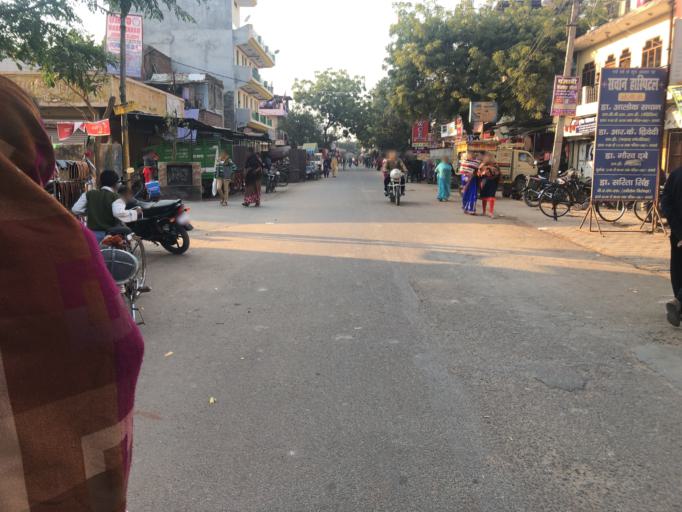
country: IN
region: Uttar Pradesh
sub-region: Kanpur
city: Kanpur
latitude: 26.4378
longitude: 80.2970
